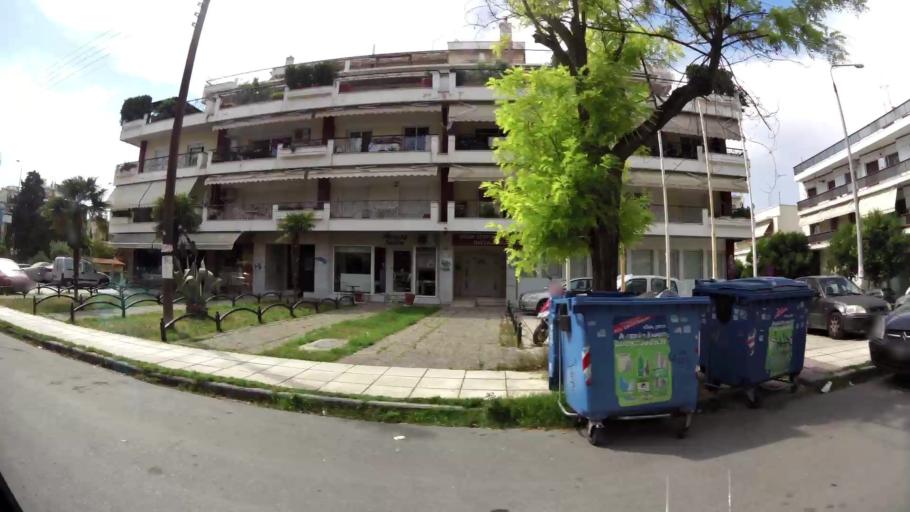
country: GR
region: Central Macedonia
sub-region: Nomos Thessalonikis
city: Kalamaria
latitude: 40.5859
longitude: 22.9475
